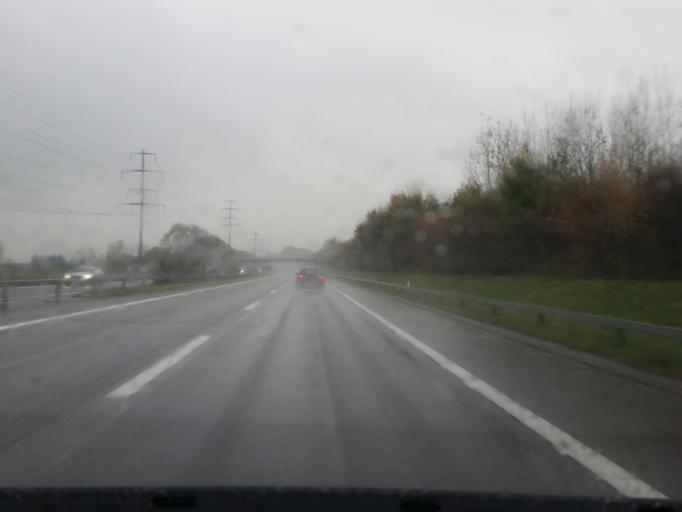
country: CH
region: Thurgau
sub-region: Frauenfeld District
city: Pfyn
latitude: 47.5879
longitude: 8.9635
